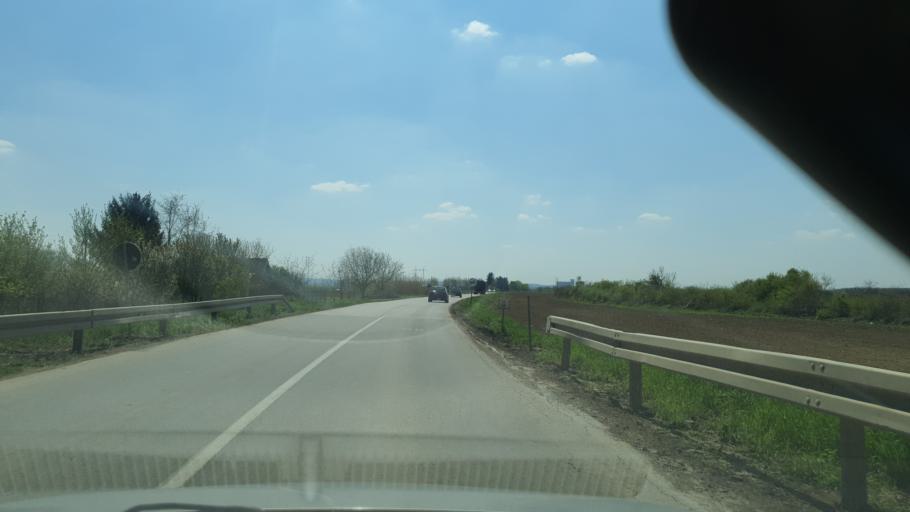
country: RS
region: Autonomna Pokrajina Vojvodina
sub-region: Juznobacki Okrug
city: Backa Palanka
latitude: 45.2766
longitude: 19.4191
